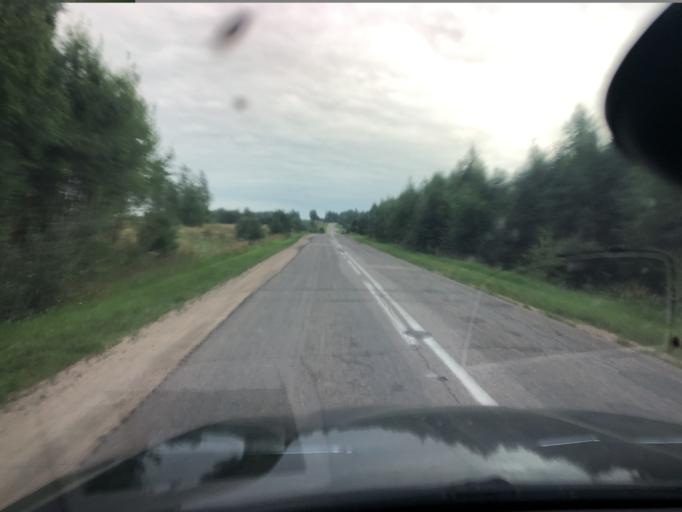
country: RU
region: Jaroslavl
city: Petrovsk
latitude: 56.9946
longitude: 39.1089
